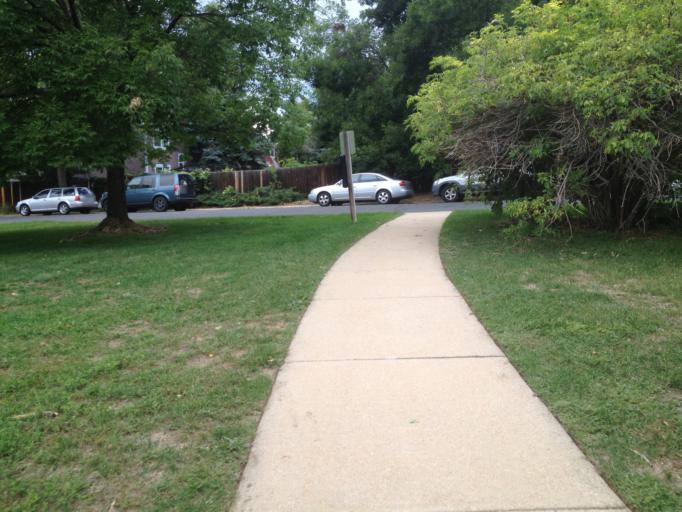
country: US
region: Colorado
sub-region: Boulder County
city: Louisville
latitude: 39.9736
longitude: -105.1454
